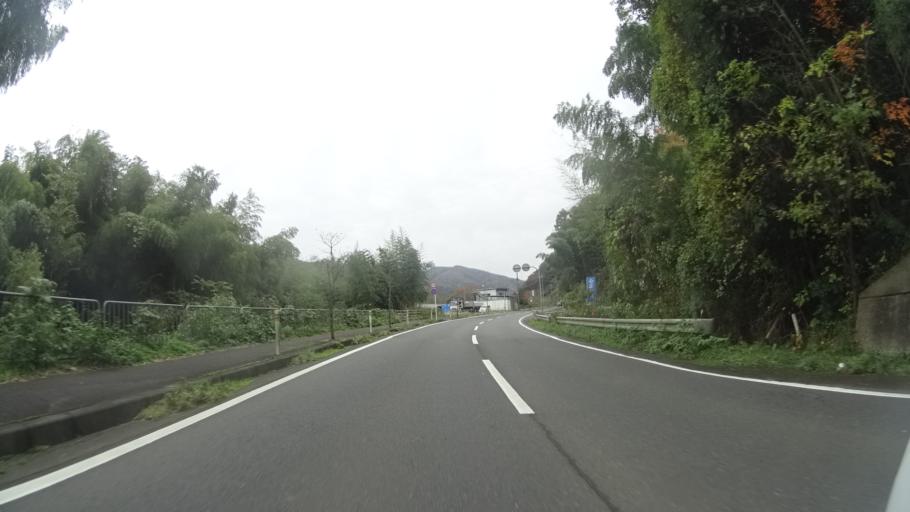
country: JP
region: Kyoto
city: Maizuru
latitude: 35.4636
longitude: 135.4124
